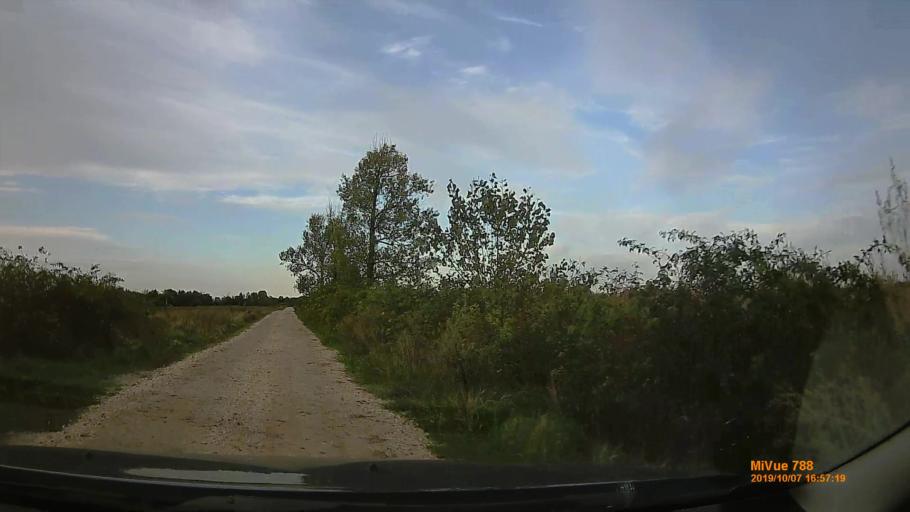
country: HU
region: Bekes
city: Szarvas
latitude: 46.8252
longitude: 20.5818
